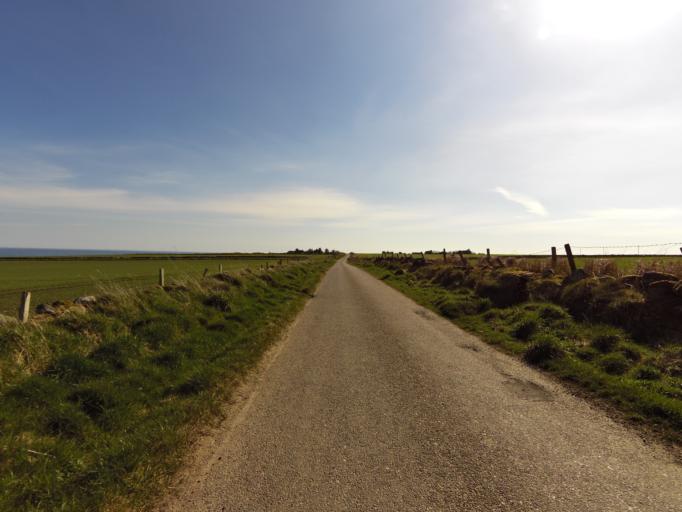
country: GB
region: Scotland
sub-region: Aberdeenshire
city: Portlethen
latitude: 57.0751
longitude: -2.1031
